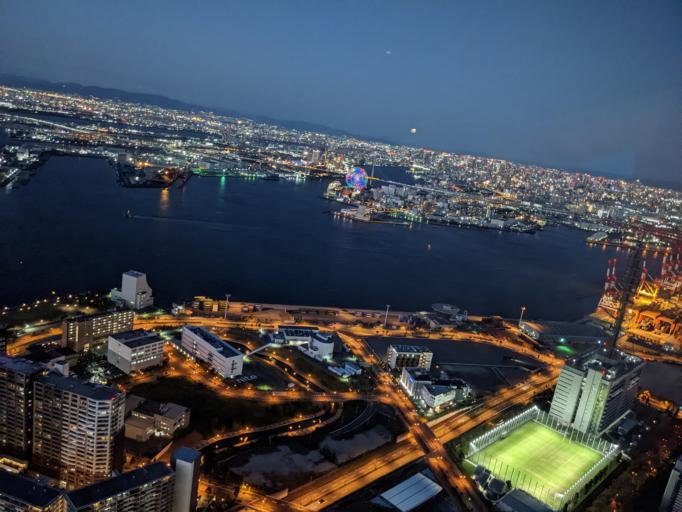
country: JP
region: Osaka
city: Sakai
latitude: 34.6382
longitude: 135.4150
